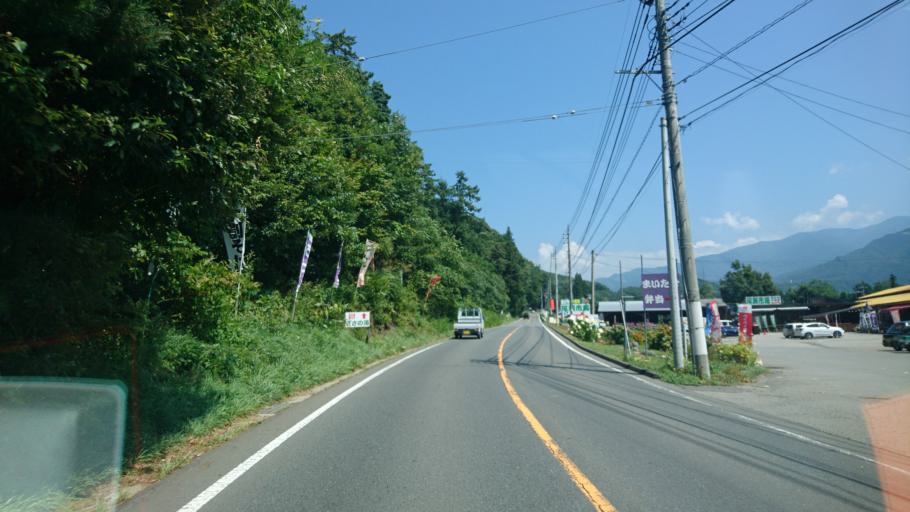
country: JP
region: Gunma
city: Numata
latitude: 36.7146
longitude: 139.2105
